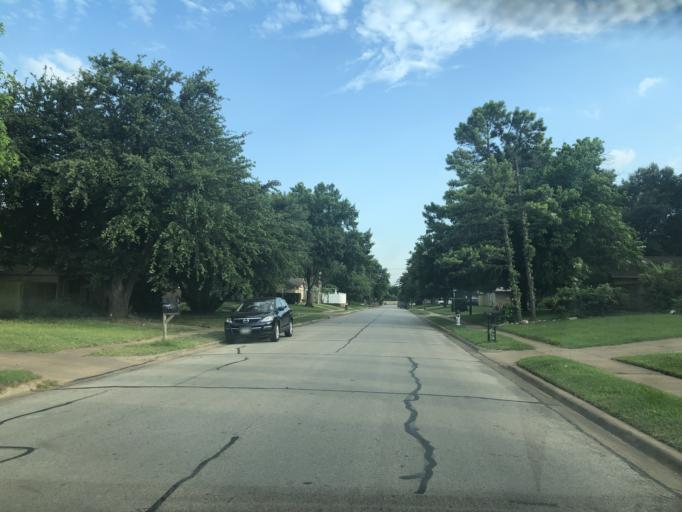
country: US
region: Texas
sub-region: Dallas County
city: Irving
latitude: 32.7888
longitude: -96.9736
